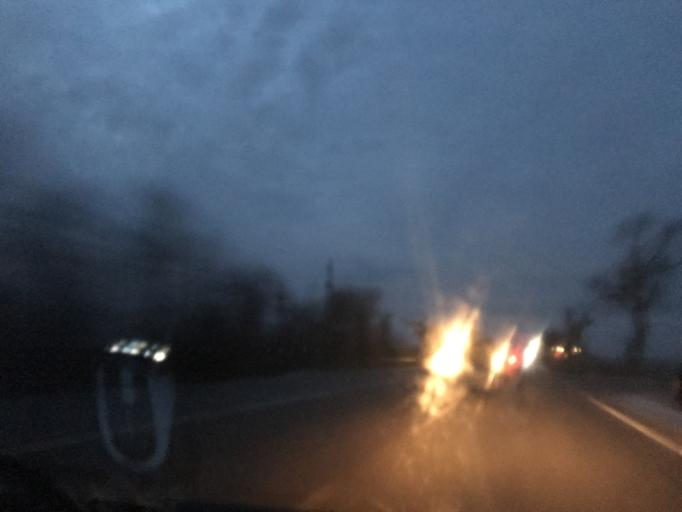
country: RU
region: Rostov
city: Bataysk
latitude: 47.0484
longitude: 39.7434
